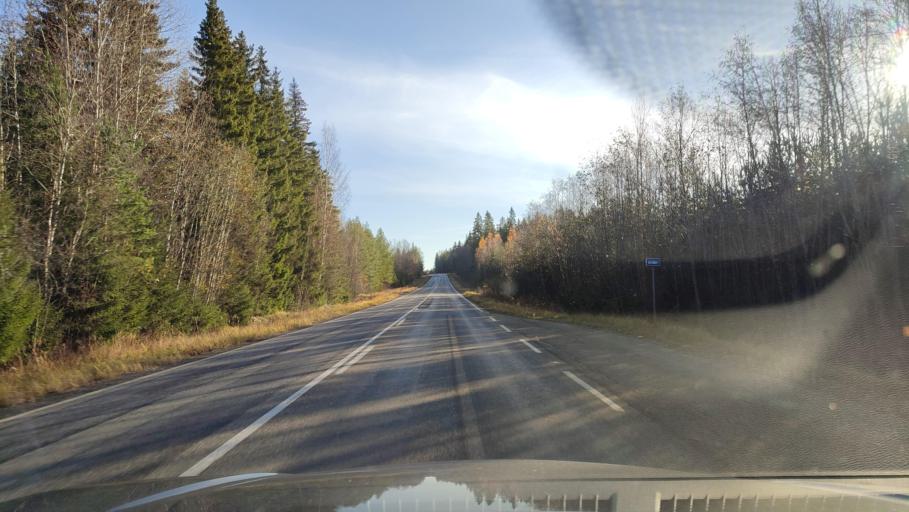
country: FI
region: Southern Ostrobothnia
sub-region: Suupohja
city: Karijoki
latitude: 62.2367
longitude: 21.6950
